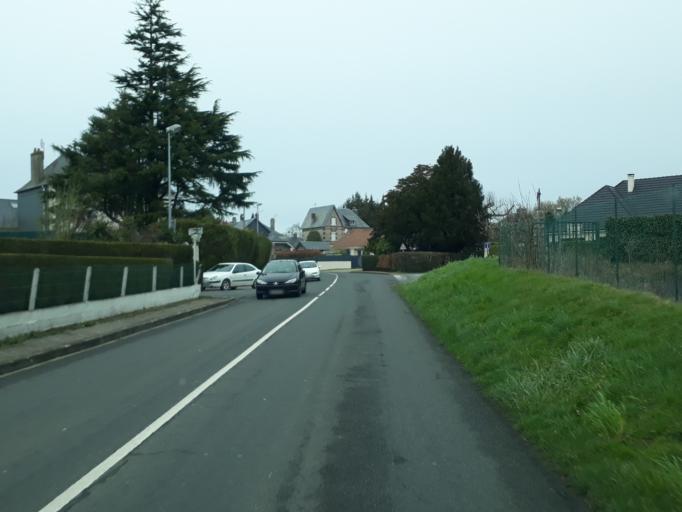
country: FR
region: Haute-Normandie
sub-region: Departement de la Seine-Maritime
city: Goderville
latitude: 49.6435
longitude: 0.3644
